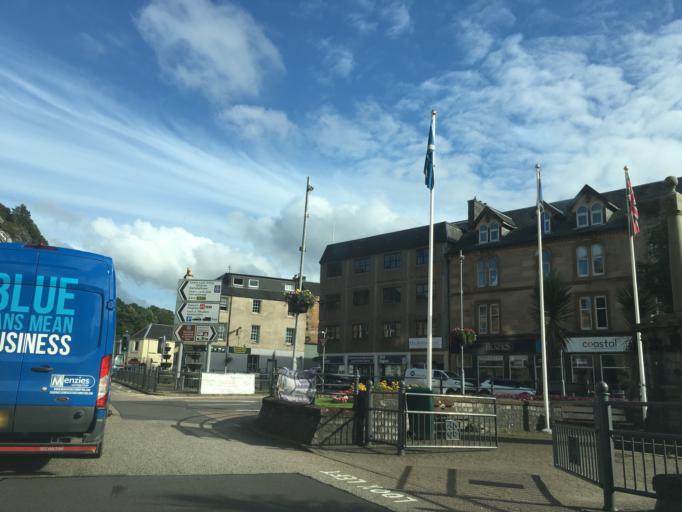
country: GB
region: Scotland
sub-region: Argyll and Bute
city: Oban
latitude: 56.4122
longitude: -5.4723
